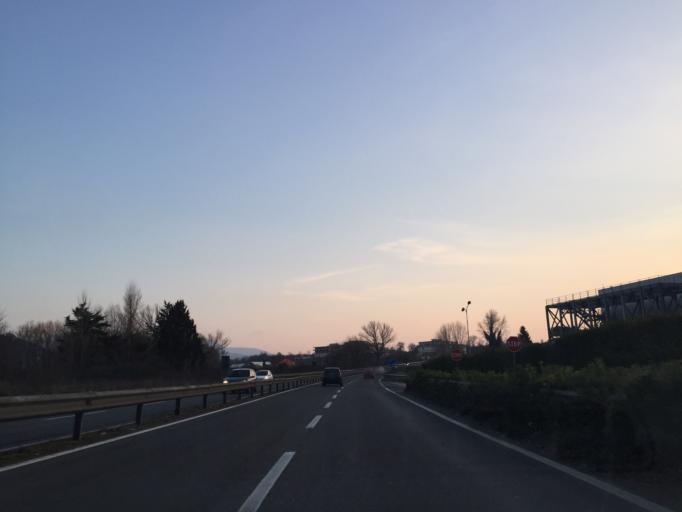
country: IT
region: Campania
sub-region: Provincia di Avellino
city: Atripalda
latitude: 40.9298
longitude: 14.8305
